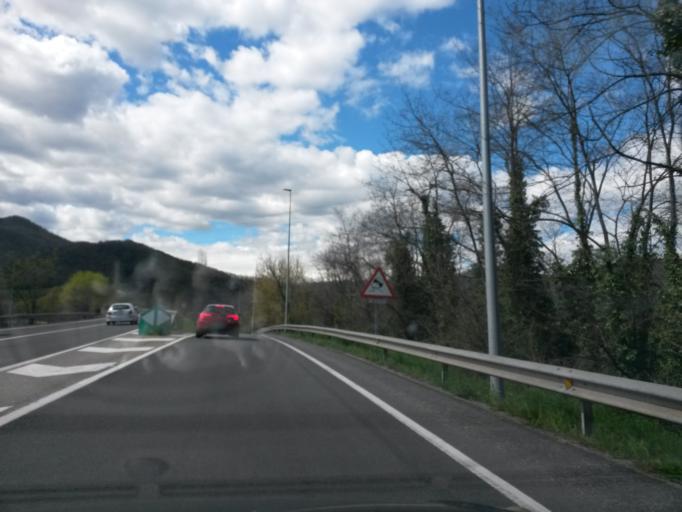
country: ES
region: Catalonia
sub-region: Provincia de Girona
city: MeteOlot
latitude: 42.1958
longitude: 2.5012
